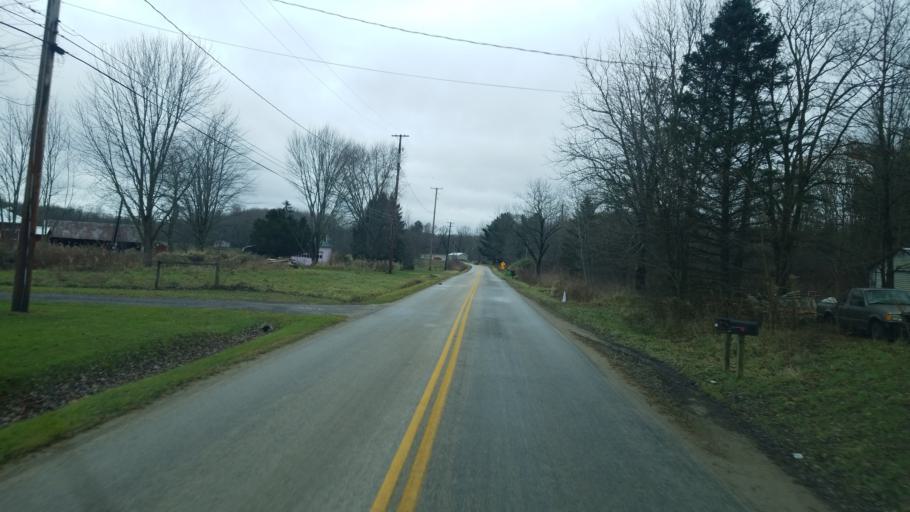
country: US
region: Ohio
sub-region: Ashtabula County
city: North Kingsville
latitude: 41.8282
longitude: -80.6235
